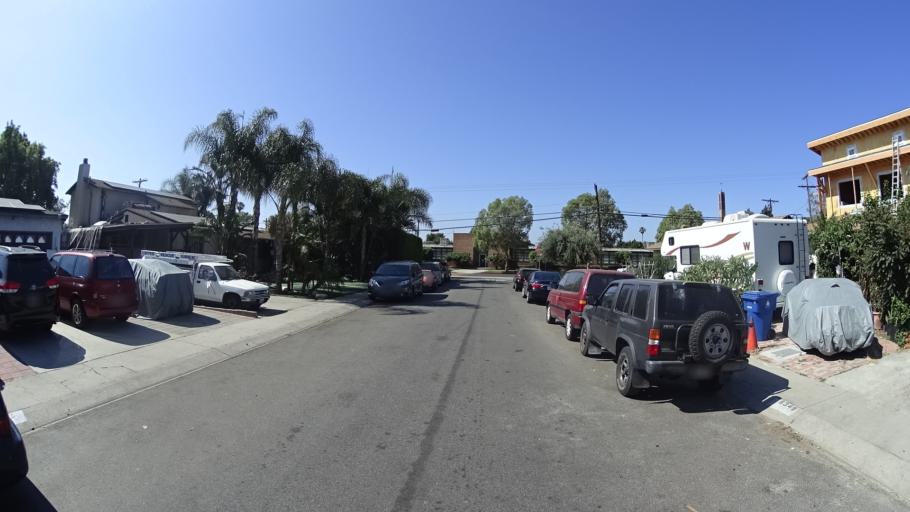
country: US
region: California
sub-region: Los Angeles County
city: Van Nuys
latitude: 34.2232
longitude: -118.4391
